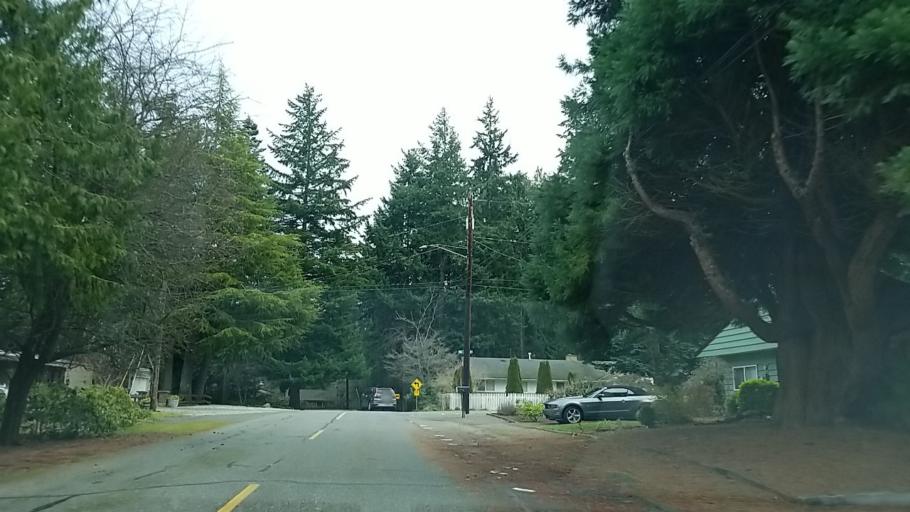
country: US
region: Washington
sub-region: Snohomish County
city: Esperance
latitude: 47.7851
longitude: -122.3625
